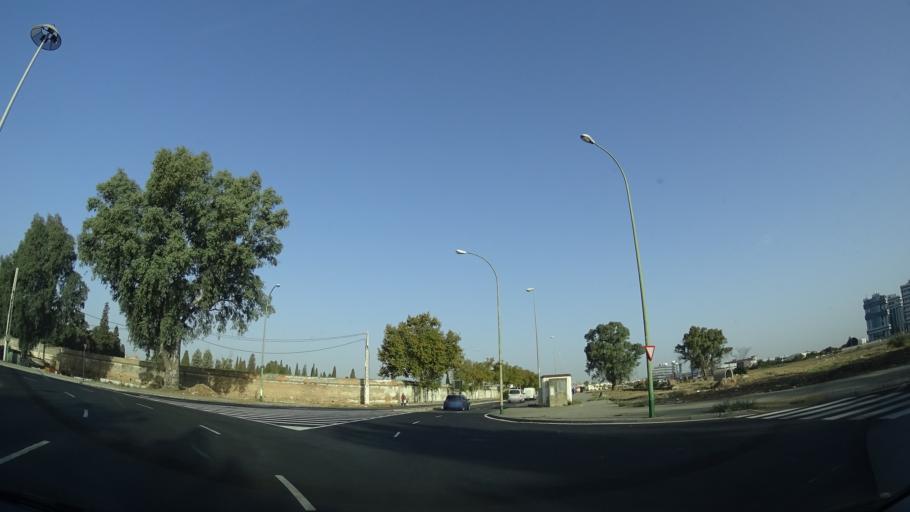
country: ES
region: Andalusia
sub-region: Provincia de Sevilla
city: Sevilla
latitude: 37.4207
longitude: -5.9766
